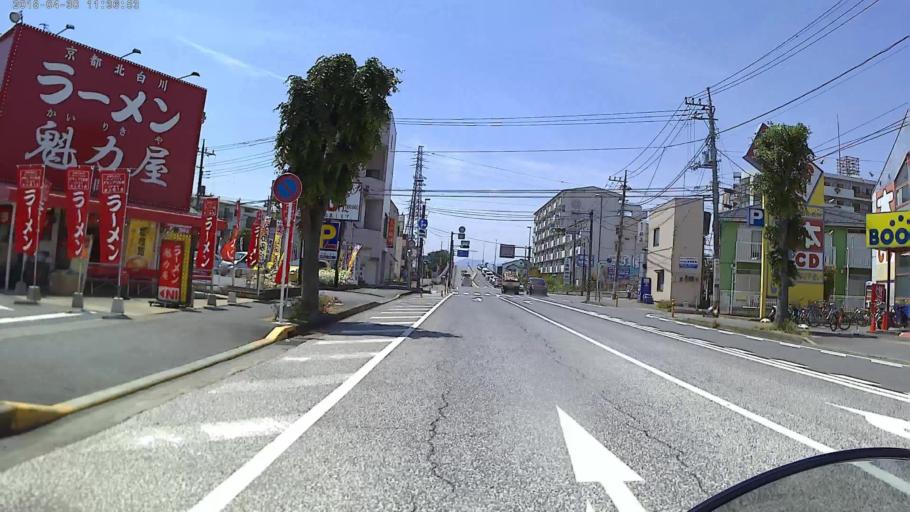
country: JP
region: Kanagawa
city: Zama
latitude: 35.4819
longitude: 139.3937
